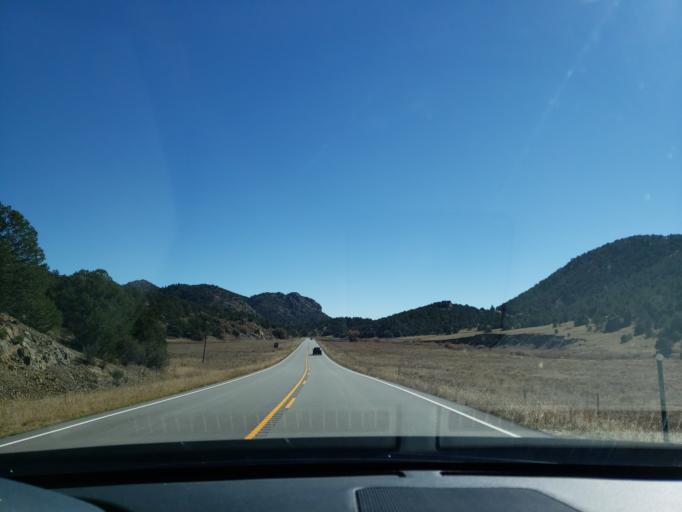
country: US
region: Colorado
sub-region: Fremont County
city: Canon City
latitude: 38.6225
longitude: -105.4552
